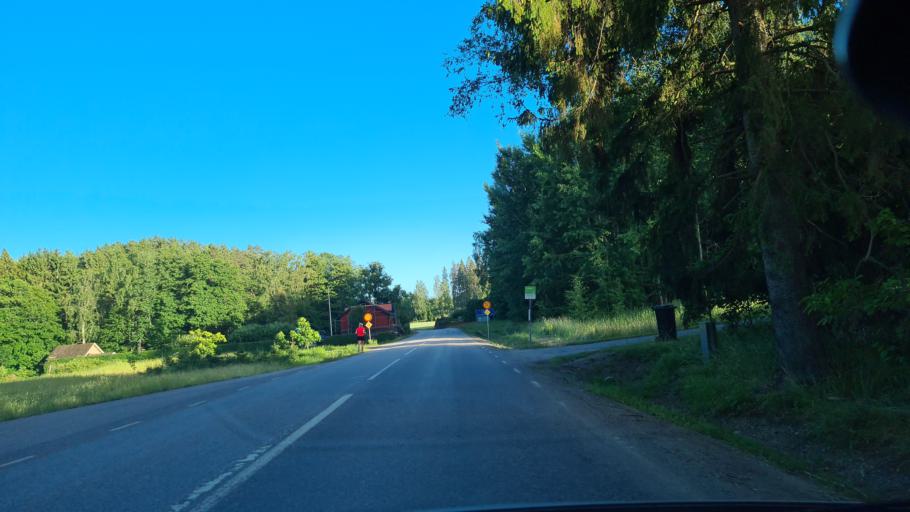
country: SE
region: Soedermanland
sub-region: Gnesta Kommun
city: Gnesta
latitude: 59.0333
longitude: 17.3323
